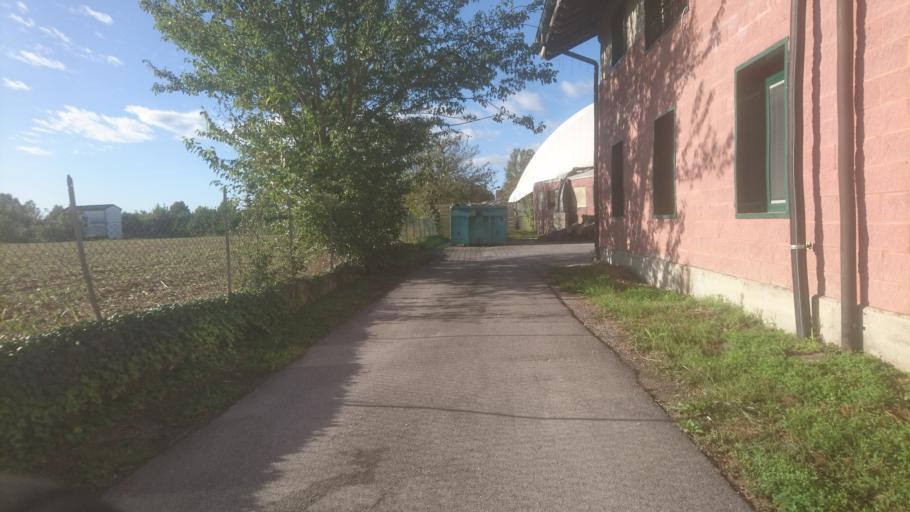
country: IT
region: Veneto
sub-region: Provincia di Padova
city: Albignasego
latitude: 45.3589
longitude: 11.8736
